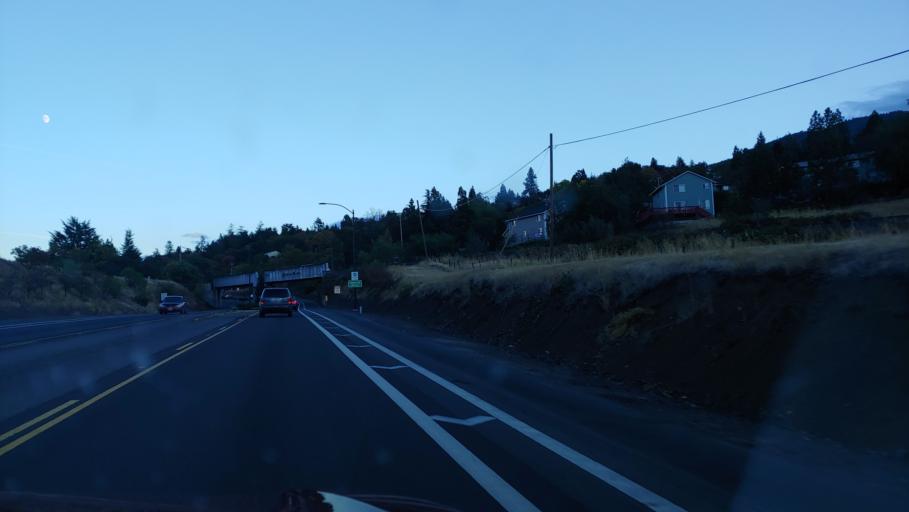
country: US
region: Oregon
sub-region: Jackson County
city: Ashland
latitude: 42.2150
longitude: -122.7316
